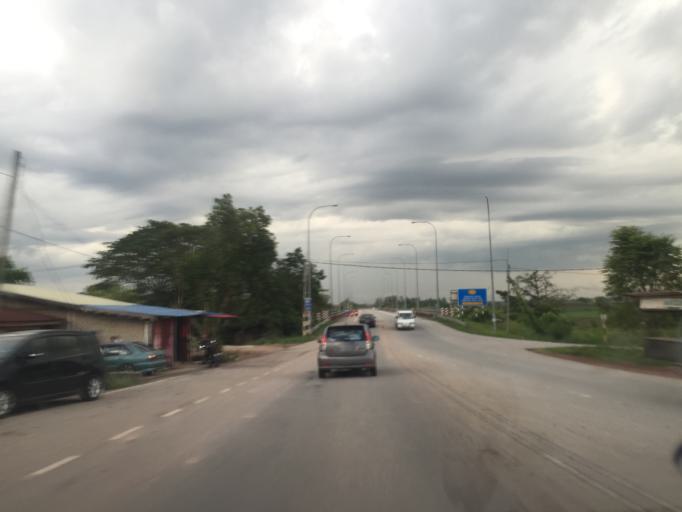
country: MY
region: Kedah
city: Sungai Petani
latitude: 5.5683
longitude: 100.5041
